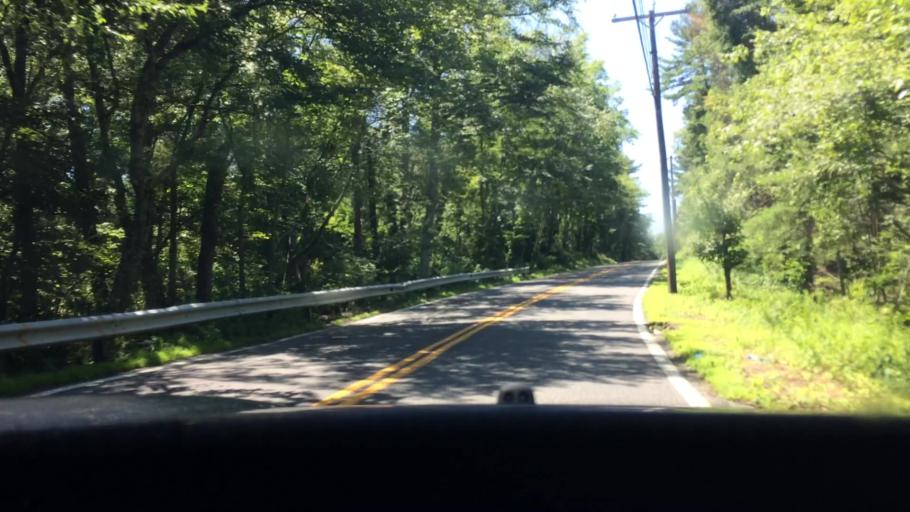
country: US
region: Rhode Island
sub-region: Providence County
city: Harrisville
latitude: 42.0072
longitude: -71.6771
